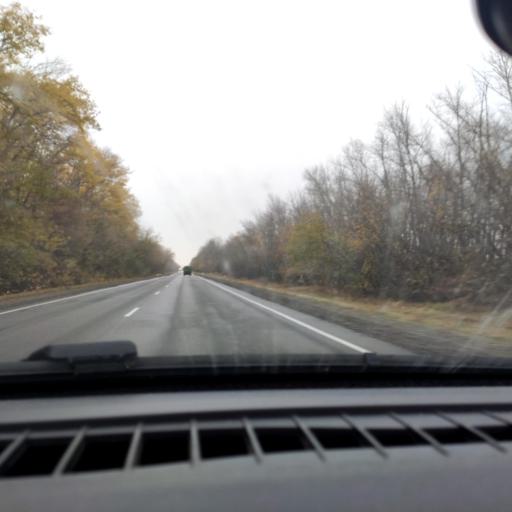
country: RU
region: Voronezj
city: Ostrogozhsk
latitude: 50.9566
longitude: 39.0338
